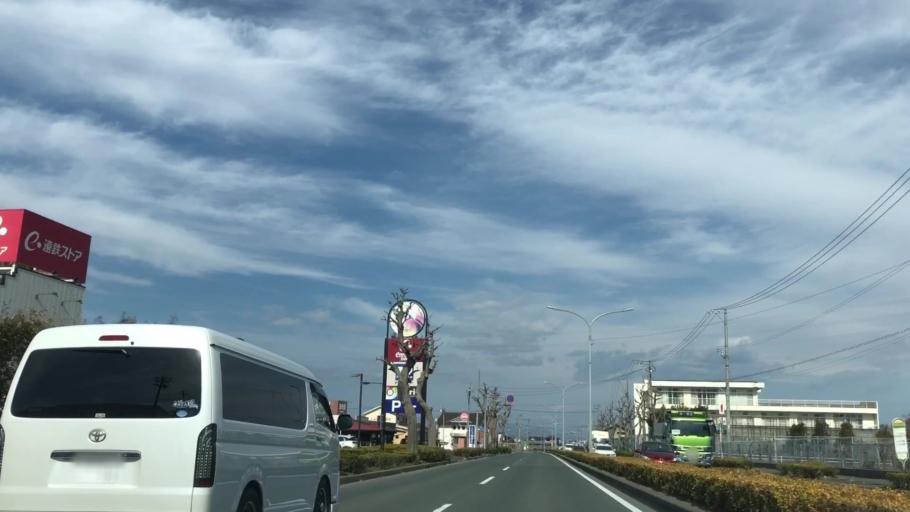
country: JP
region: Shizuoka
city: Hamamatsu
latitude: 34.7319
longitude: 137.6586
